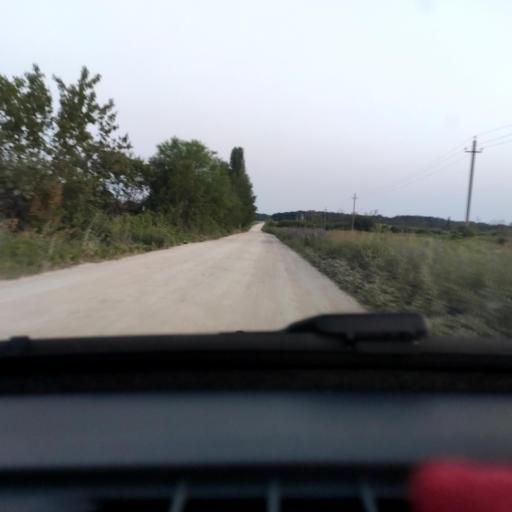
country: RU
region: Voronezj
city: Podgornoye
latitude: 51.8632
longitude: 39.0995
